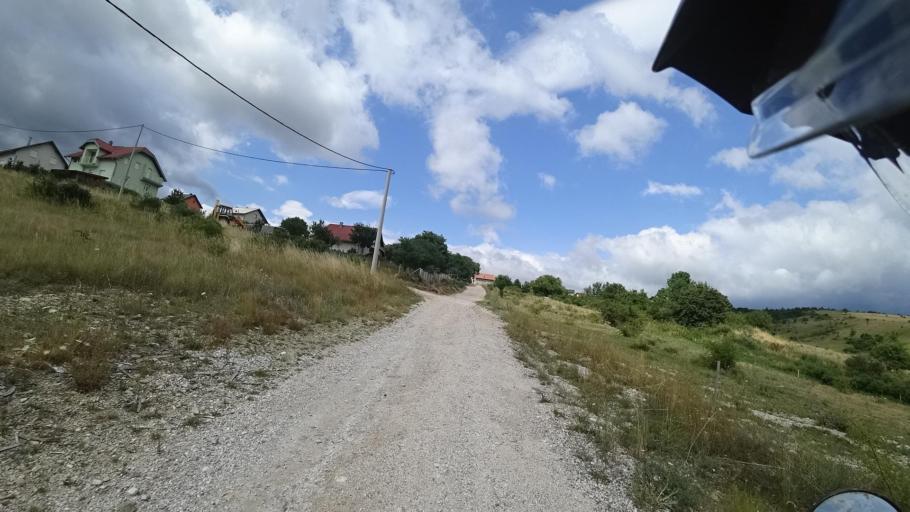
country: HR
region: Zadarska
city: Gracac
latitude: 44.5271
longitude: 15.7655
